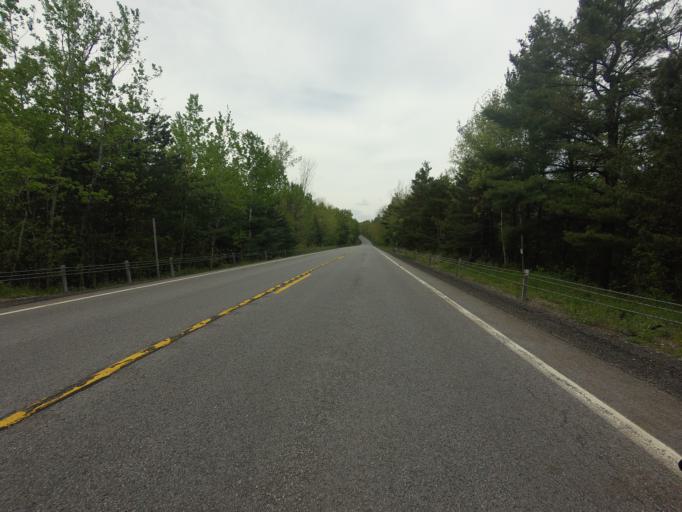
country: US
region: New York
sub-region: St. Lawrence County
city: Hannawa Falls
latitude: 44.6422
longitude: -74.7831
